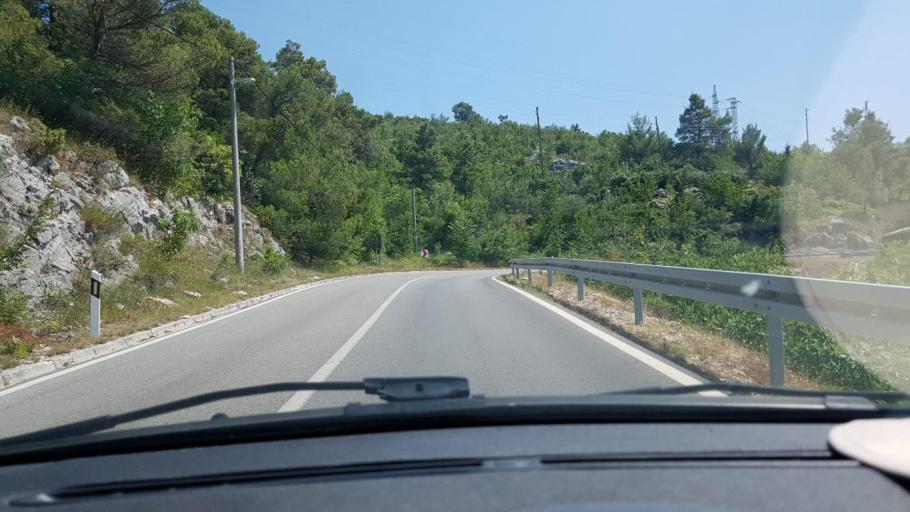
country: HR
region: Splitsko-Dalmatinska
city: Vrgorac
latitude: 43.1998
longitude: 17.3772
